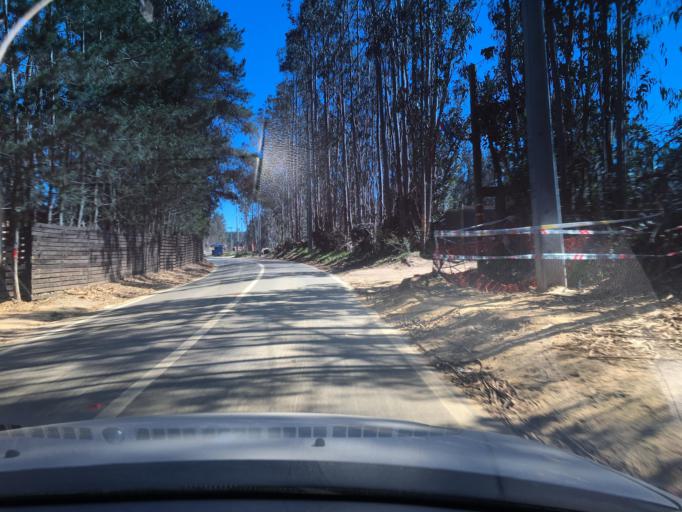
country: CL
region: Valparaiso
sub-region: San Antonio Province
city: El Tabo
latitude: -33.4243
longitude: -71.6319
